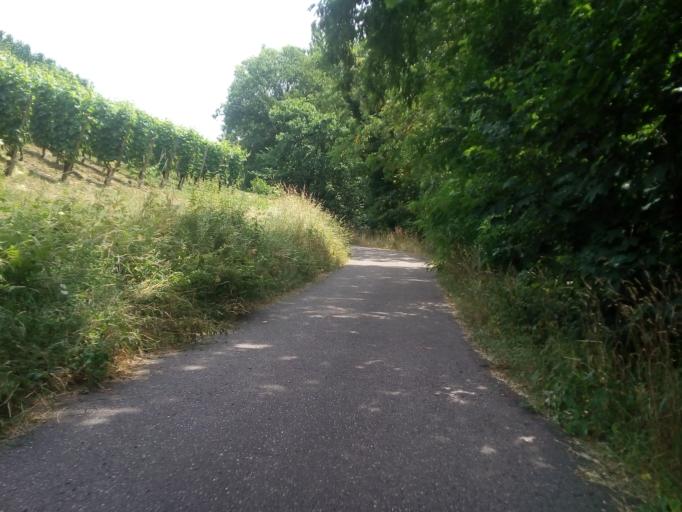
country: DE
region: Baden-Wuerttemberg
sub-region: Freiburg Region
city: Achern
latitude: 48.6071
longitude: 8.0918
